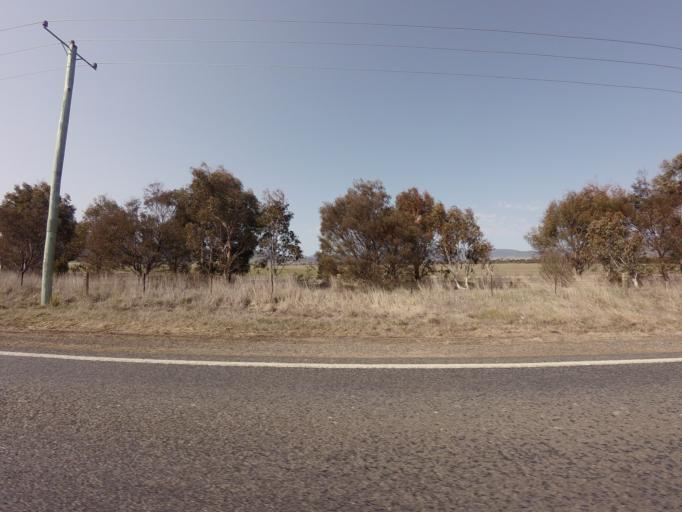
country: AU
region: Tasmania
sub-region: Northern Midlands
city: Evandale
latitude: -41.7921
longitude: 147.7108
